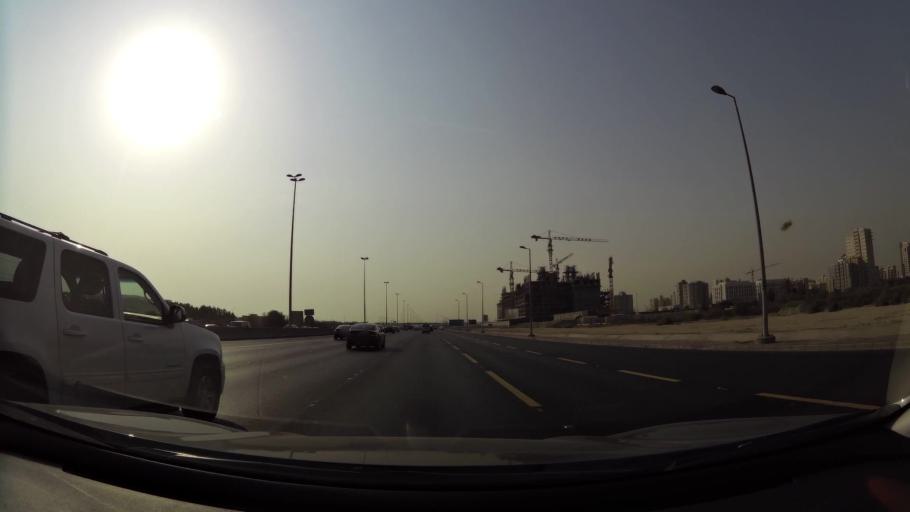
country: KW
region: Mubarak al Kabir
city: Sabah as Salim
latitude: 29.2555
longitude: 48.0893
